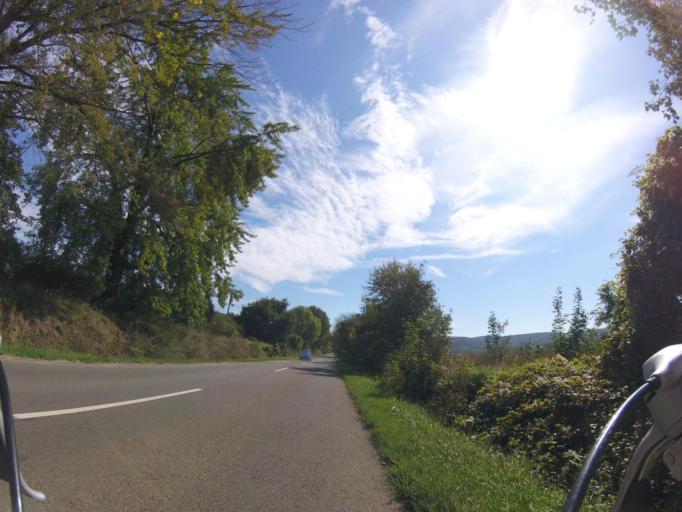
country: HU
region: Komarom-Esztergom
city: Esztergom
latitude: 47.8774
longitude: 18.7827
